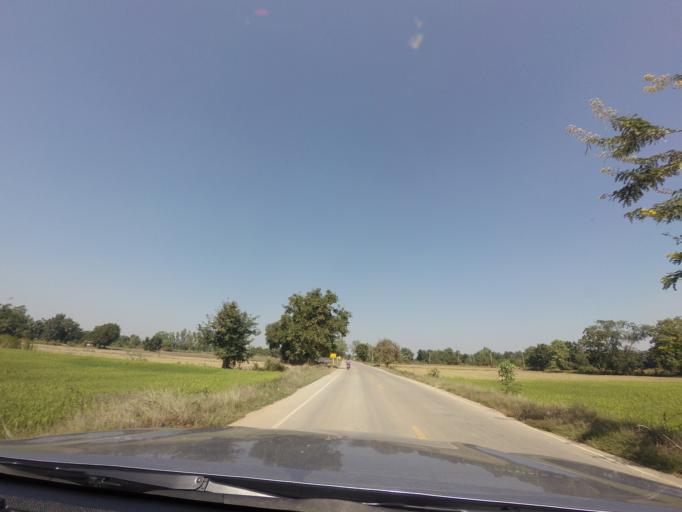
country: TH
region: Sukhothai
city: Si Samrong
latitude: 17.1475
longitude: 99.7696
